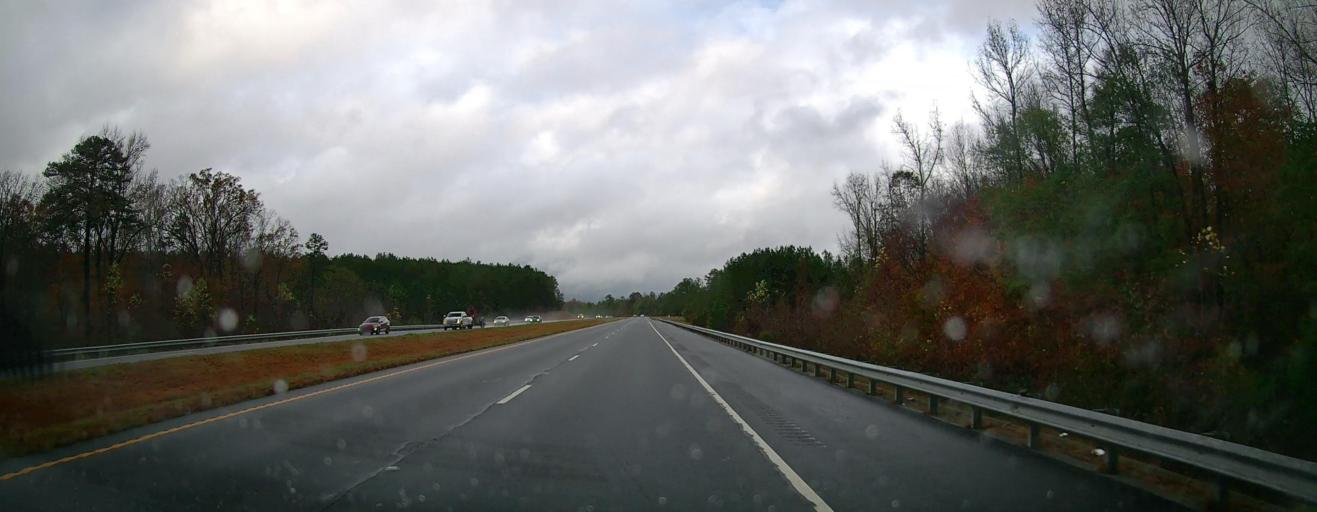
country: US
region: Georgia
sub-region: Jackson County
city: Nicholson
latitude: 34.0714
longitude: -83.4242
